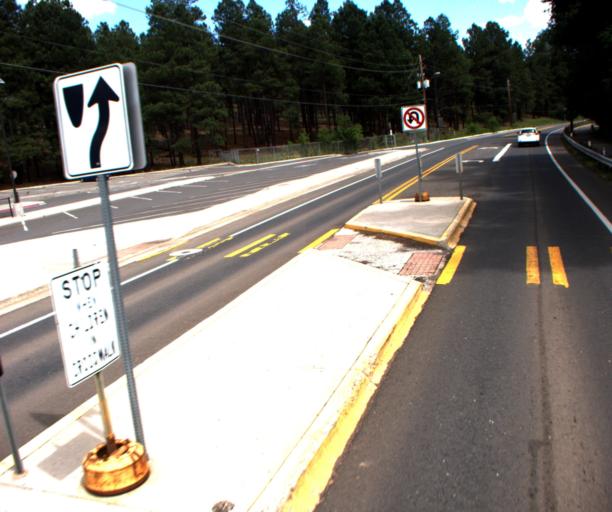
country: US
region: Arizona
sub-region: Coconino County
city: Flagstaff
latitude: 35.2223
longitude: -111.6540
